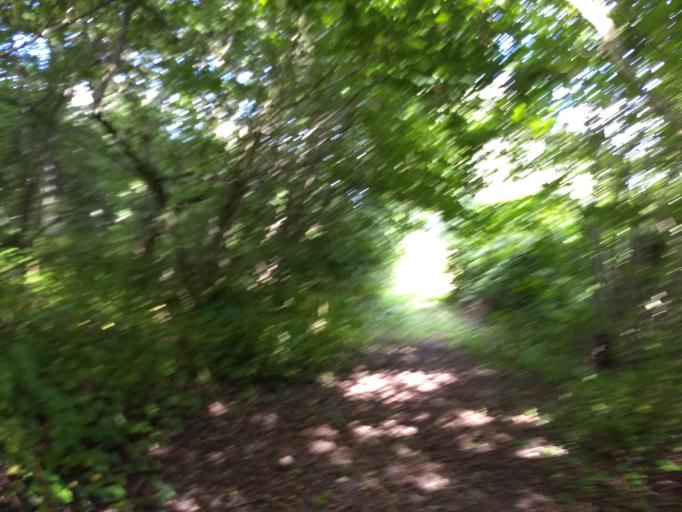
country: GB
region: England
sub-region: Isle of Wight
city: Shalfleet
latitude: 50.6800
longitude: -1.4262
